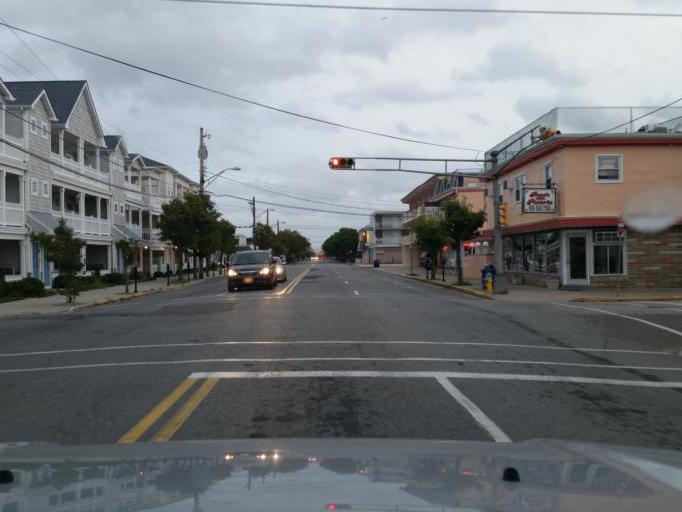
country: US
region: New Jersey
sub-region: Cape May County
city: Wildwood
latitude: 38.9817
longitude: -74.8209
